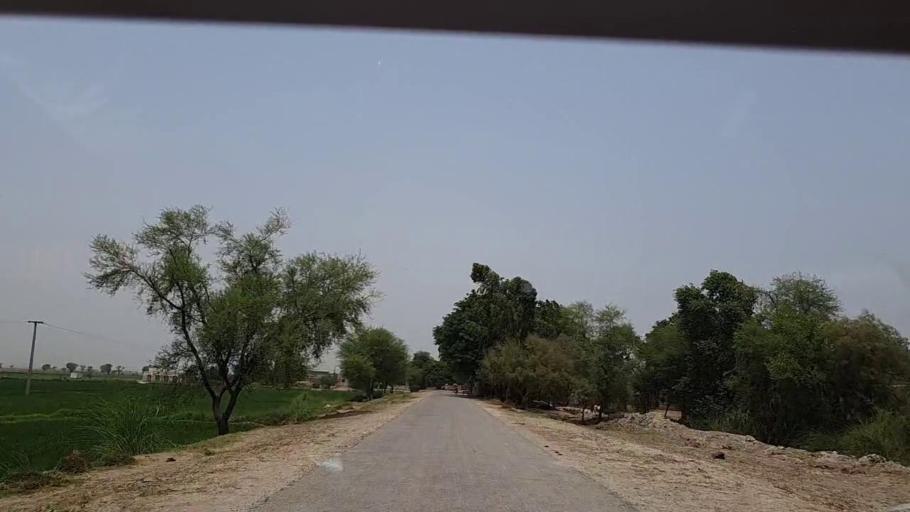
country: PK
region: Sindh
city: Khairpur Nathan Shah
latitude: 27.0159
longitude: 67.6701
